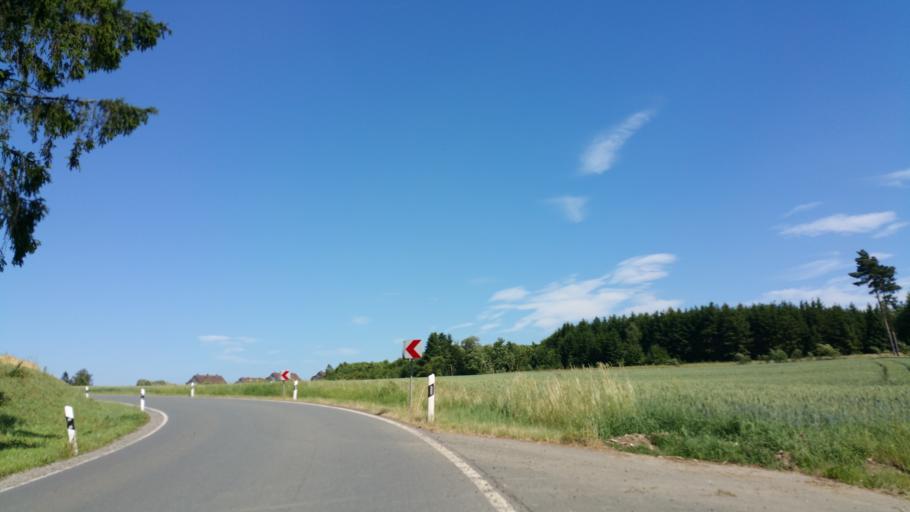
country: DE
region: Bavaria
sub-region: Upper Franconia
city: Koditz
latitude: 50.3454
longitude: 11.8630
